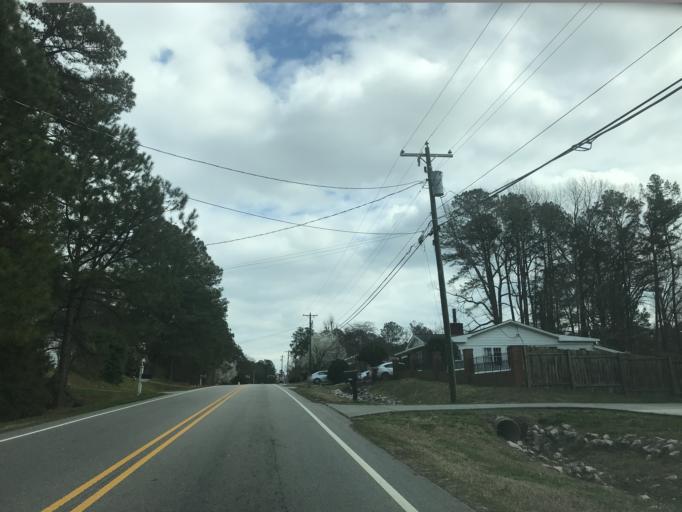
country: US
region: North Carolina
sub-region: Wake County
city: Raleigh
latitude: 35.8111
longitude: -78.5809
